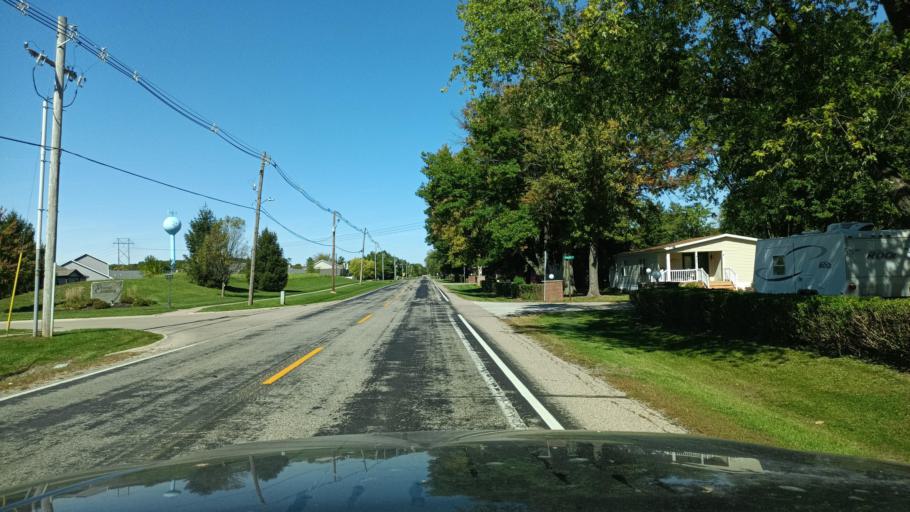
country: US
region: Illinois
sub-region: Champaign County
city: Lake of the Woods
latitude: 40.2008
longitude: -88.3653
